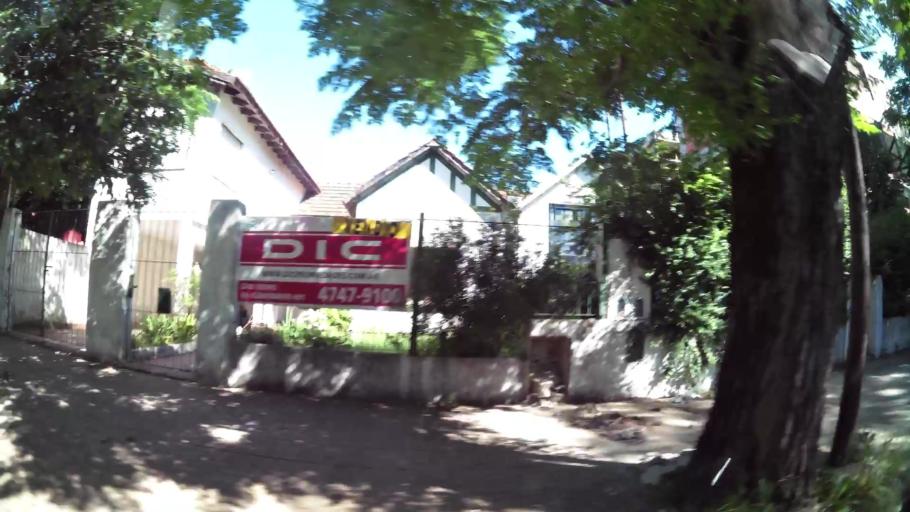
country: AR
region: Buenos Aires
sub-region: Partido de San Isidro
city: San Isidro
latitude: -34.4626
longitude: -58.5282
